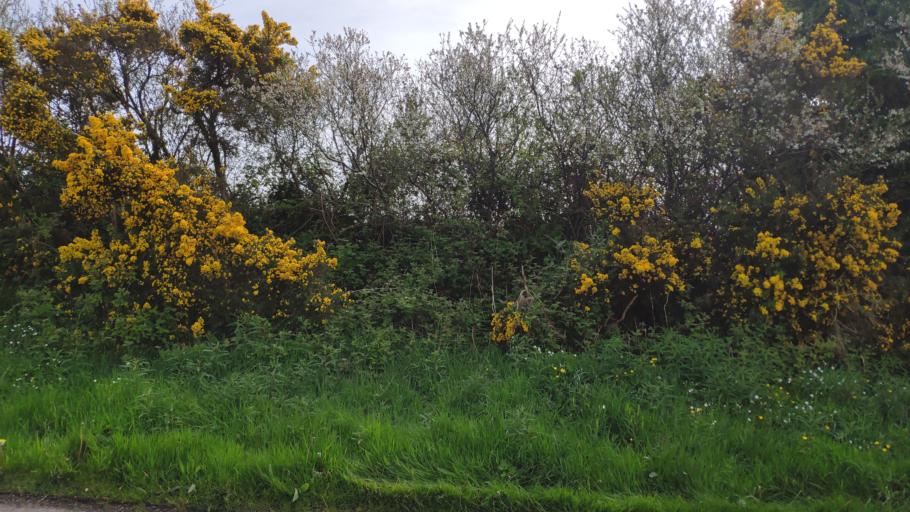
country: IE
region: Munster
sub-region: County Cork
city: Blarney
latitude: 51.9669
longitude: -8.5142
